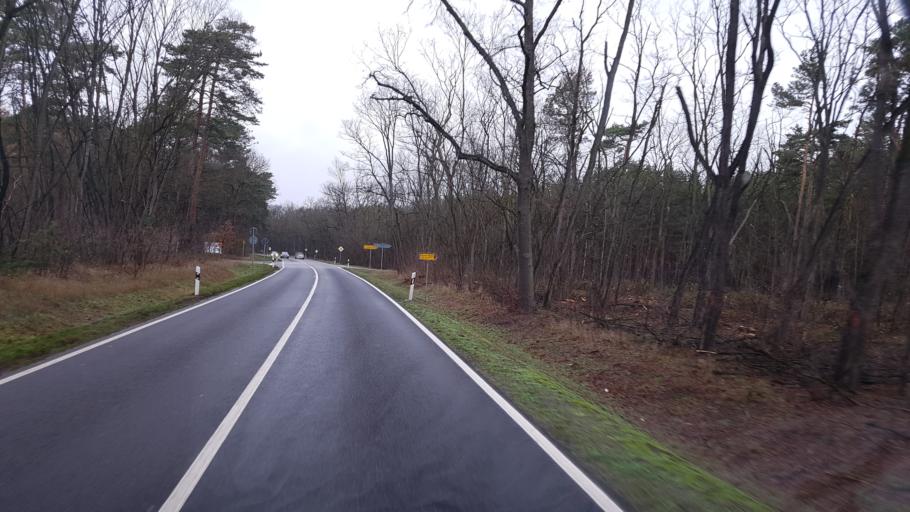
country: DE
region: Brandenburg
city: Calau
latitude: 51.7226
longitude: 14.0088
